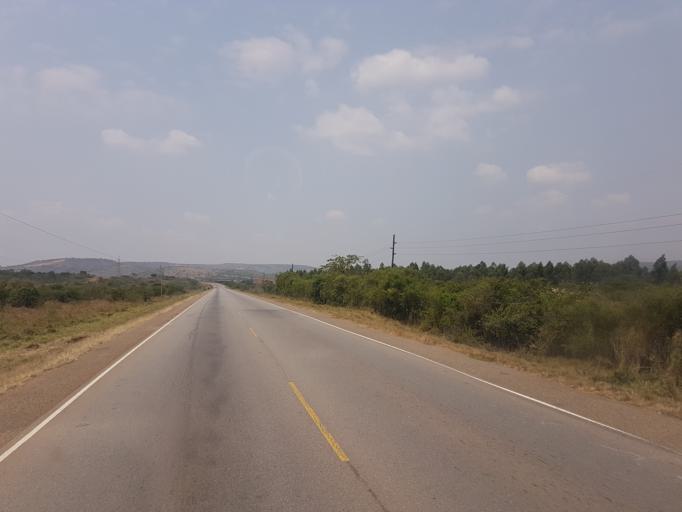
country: UG
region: Western Region
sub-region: Mbarara District
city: Mbarara
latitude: -0.5098
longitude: 30.8330
